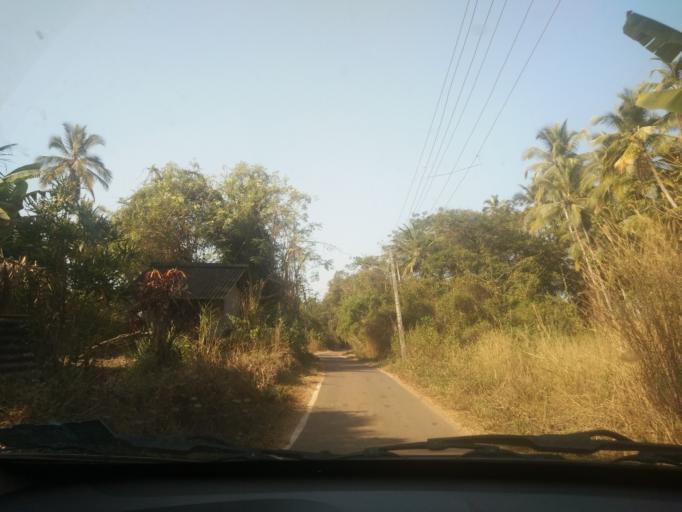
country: IN
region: Goa
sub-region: South Goa
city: Sancoale
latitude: 15.3523
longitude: 73.8895
